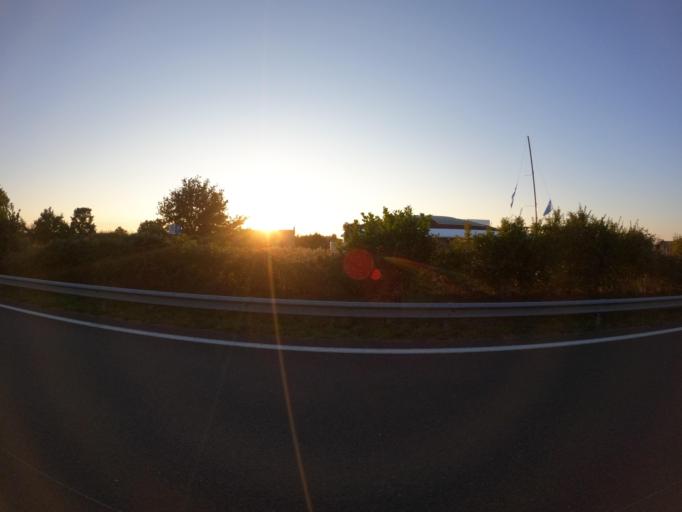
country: FR
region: Pays de la Loire
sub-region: Departement de la Vendee
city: Belleville-sur-Vie
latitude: 46.7478
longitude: -1.4304
